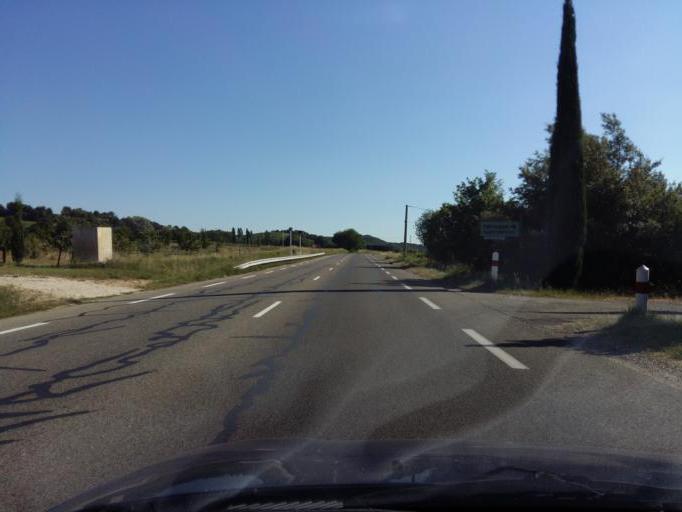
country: FR
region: Provence-Alpes-Cote d'Azur
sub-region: Departement du Vaucluse
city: Valreas
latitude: 44.3631
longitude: 4.9739
